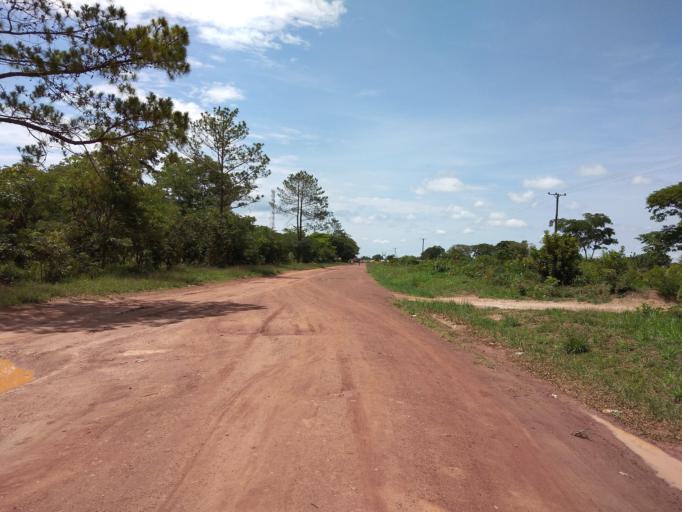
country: ZM
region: Copperbelt
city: Luanshya
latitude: -13.4737
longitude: 28.6762
